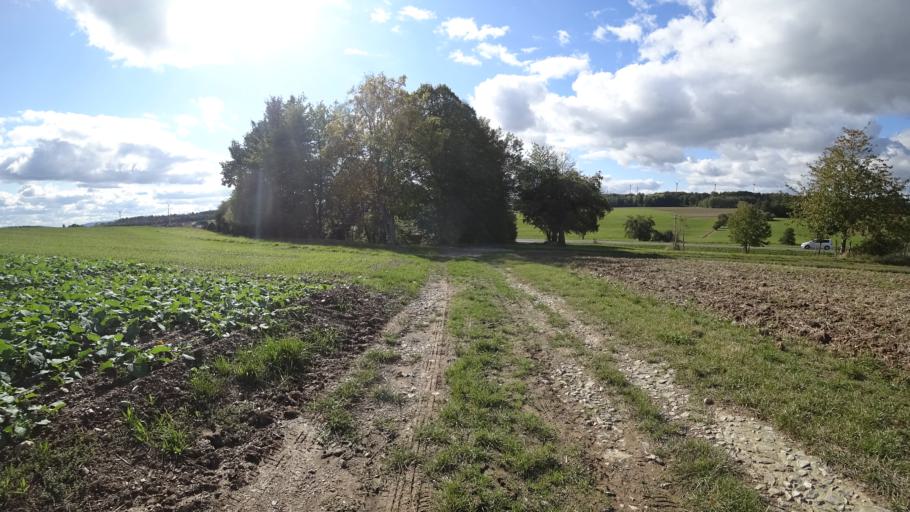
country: DE
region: Rheinland-Pfalz
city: Reich
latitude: 50.0061
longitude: 7.4319
